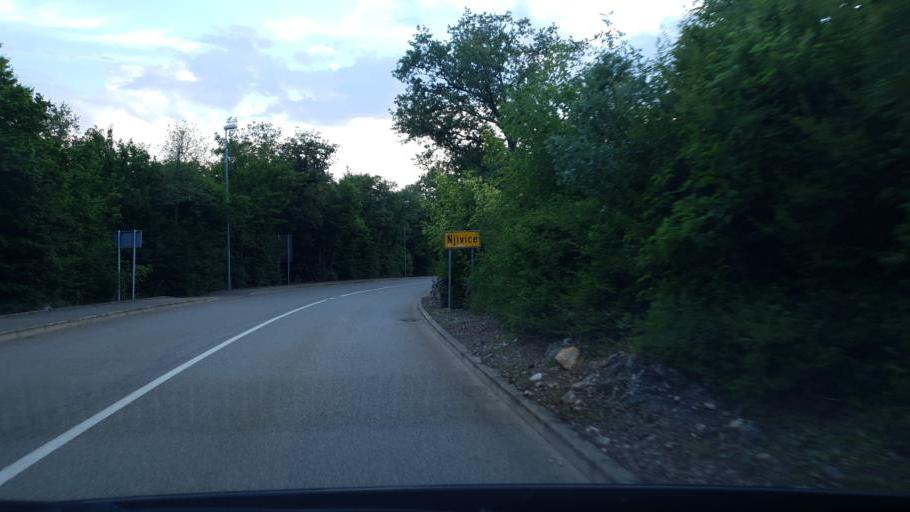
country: HR
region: Primorsko-Goranska
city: Njivice
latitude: 45.1633
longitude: 14.5484
